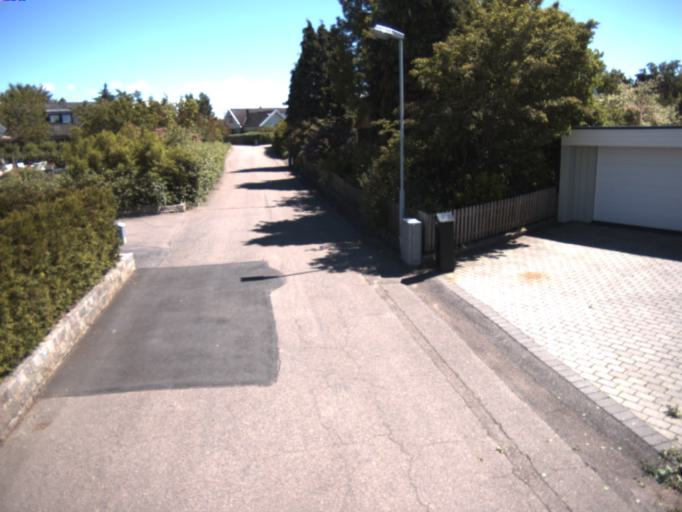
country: SE
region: Skane
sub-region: Helsingborg
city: Rydeback
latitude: 55.9738
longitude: 12.7721
